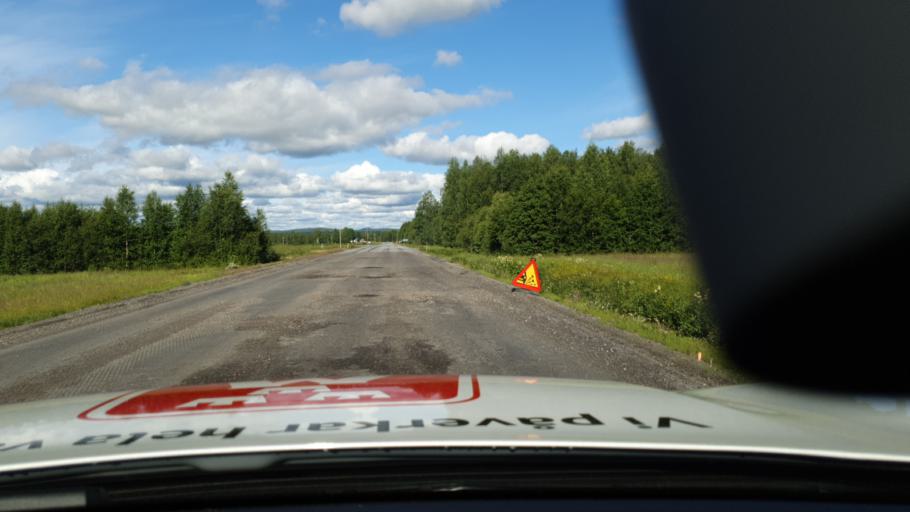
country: SE
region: Norrbotten
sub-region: Bodens Kommun
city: Boden
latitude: 65.8502
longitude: 21.5288
